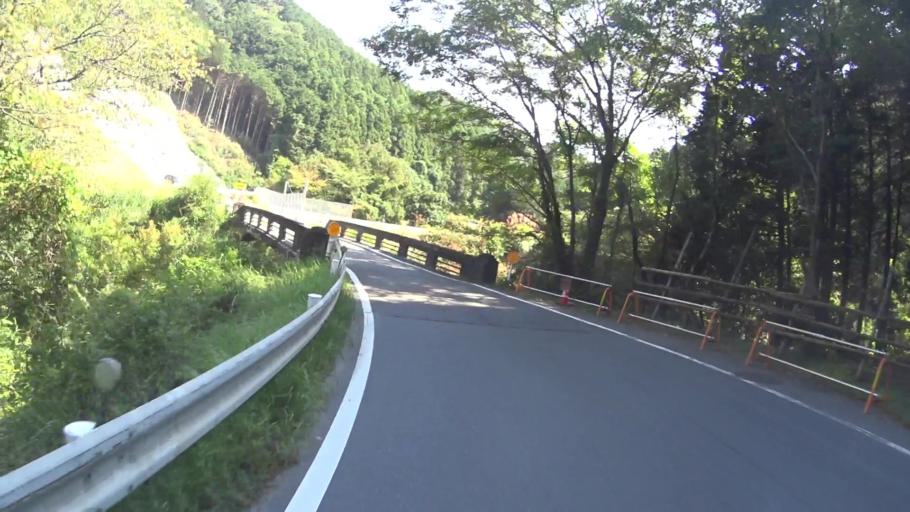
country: JP
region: Kyoto
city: Kameoka
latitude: 34.9838
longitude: 135.5741
